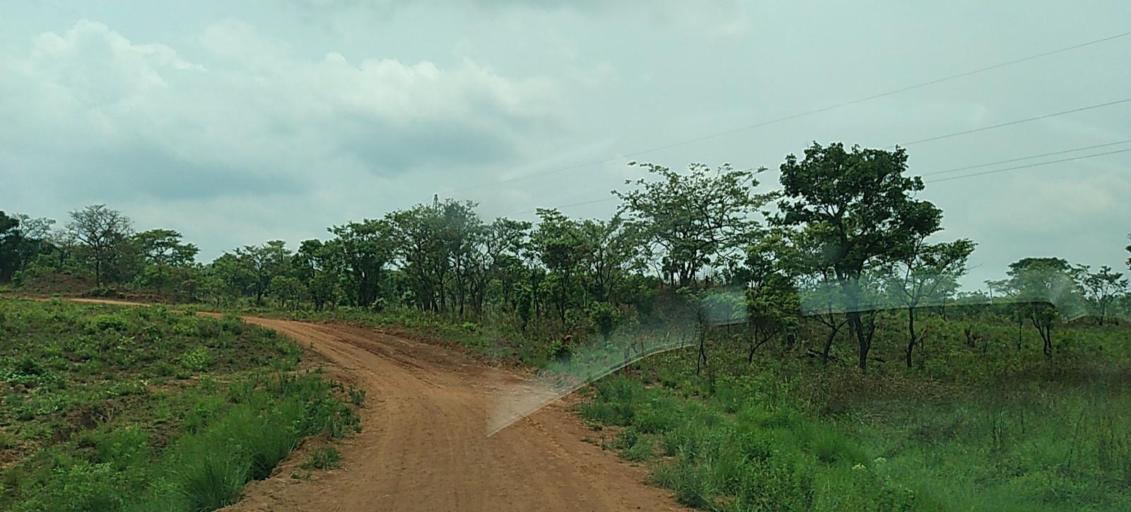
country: ZM
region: North-Western
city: Mwinilunga
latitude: -11.4576
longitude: 24.7600
